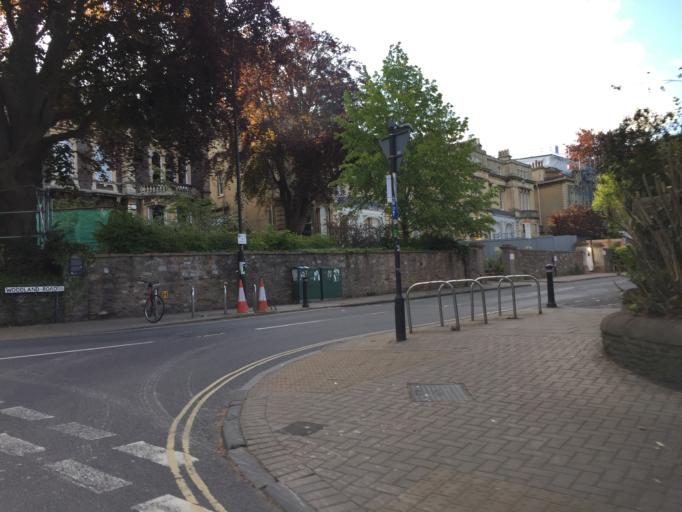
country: GB
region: England
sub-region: Bristol
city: Bristol
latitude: 51.4610
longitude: -2.6051
